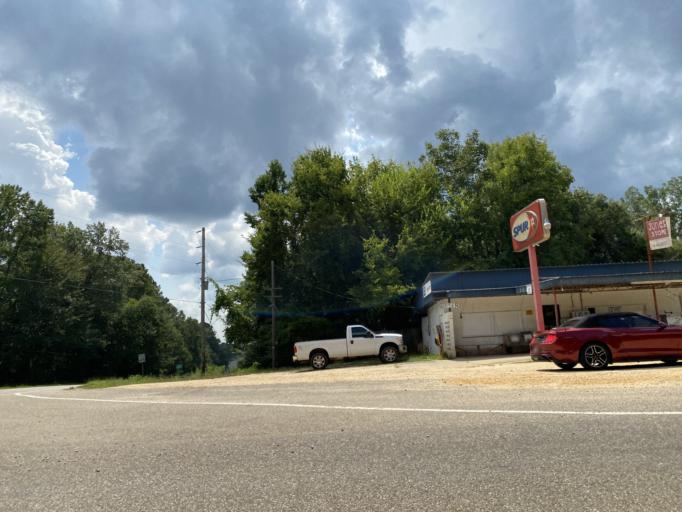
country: US
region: Alabama
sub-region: Lowndes County
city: Mosses
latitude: 32.0620
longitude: -86.7014
